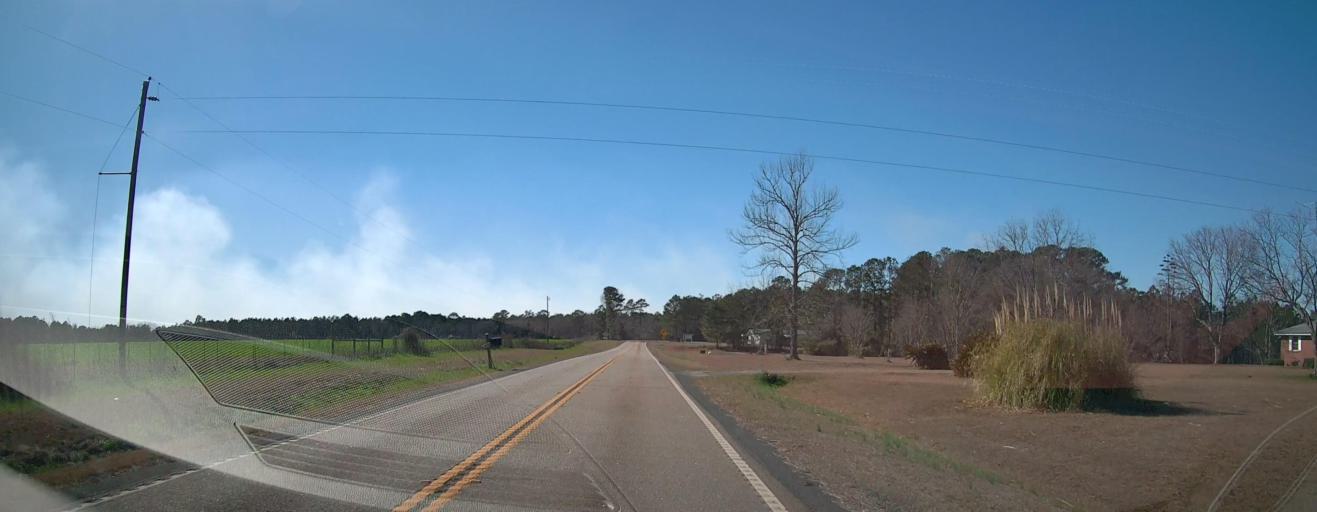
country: US
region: Georgia
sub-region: Schley County
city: Ellaville
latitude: 32.1894
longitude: -84.2055
